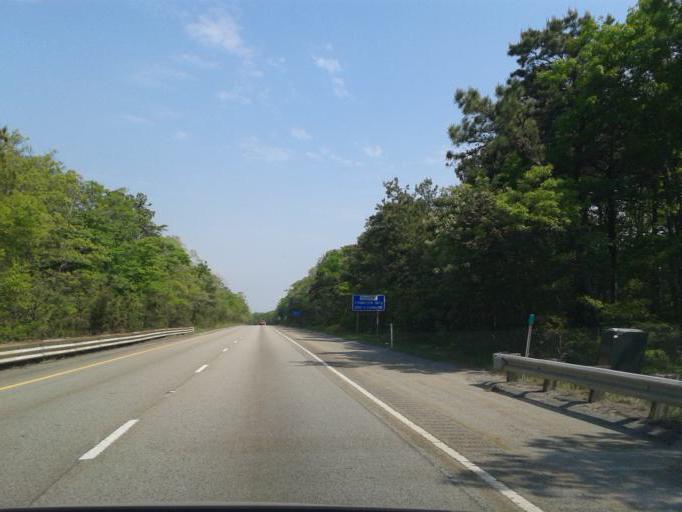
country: US
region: Massachusetts
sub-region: Barnstable County
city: Sagamore
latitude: 41.7918
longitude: -70.5445
